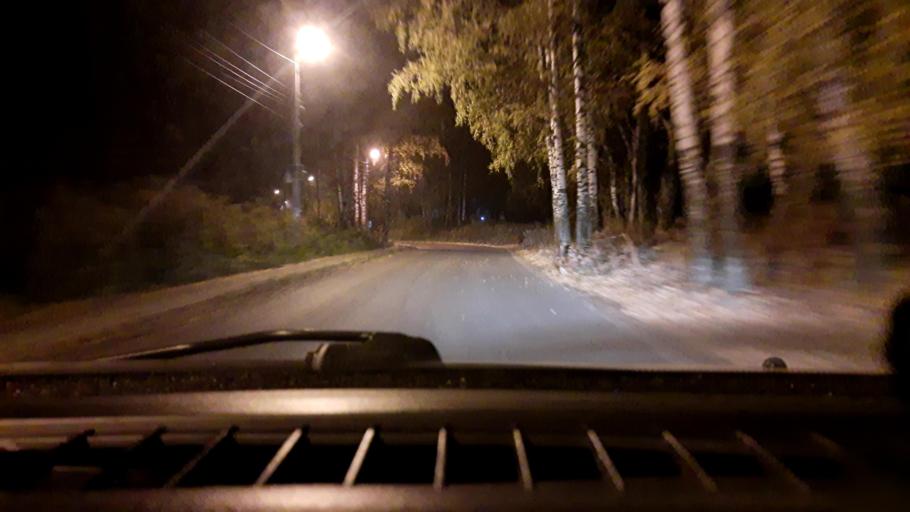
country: RU
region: Nizjnij Novgorod
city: Afonino
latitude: 56.2124
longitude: 44.0953
